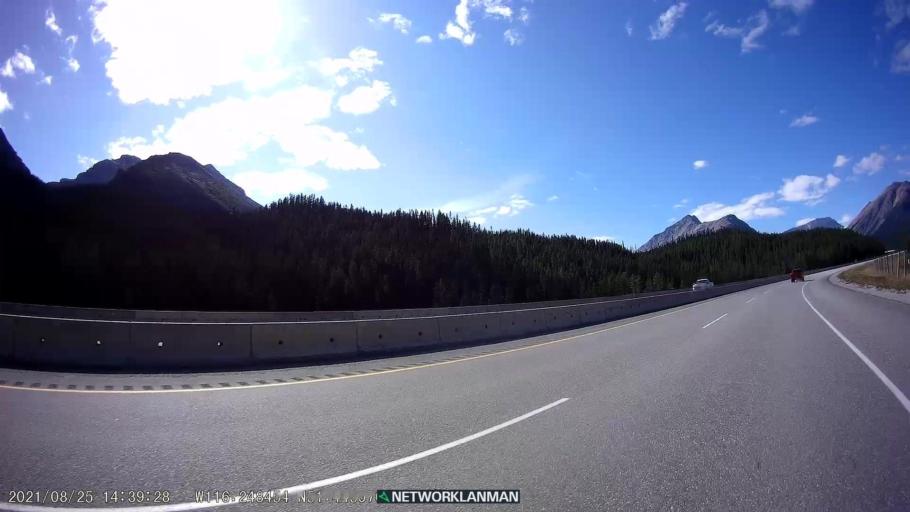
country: CA
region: Alberta
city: Lake Louise
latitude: 51.4450
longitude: -116.2456
